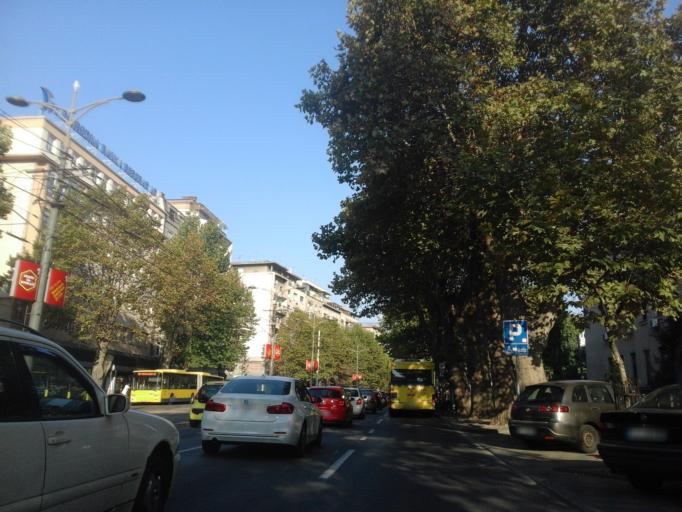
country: RS
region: Central Serbia
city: Belgrade
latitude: 44.8066
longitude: 20.4729
